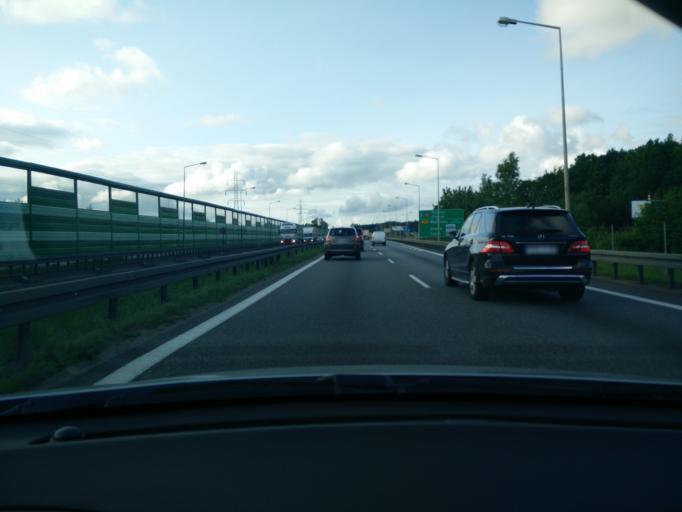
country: PL
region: Pomeranian Voivodeship
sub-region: Gdynia
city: Wielki Kack
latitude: 54.4222
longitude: 18.4875
